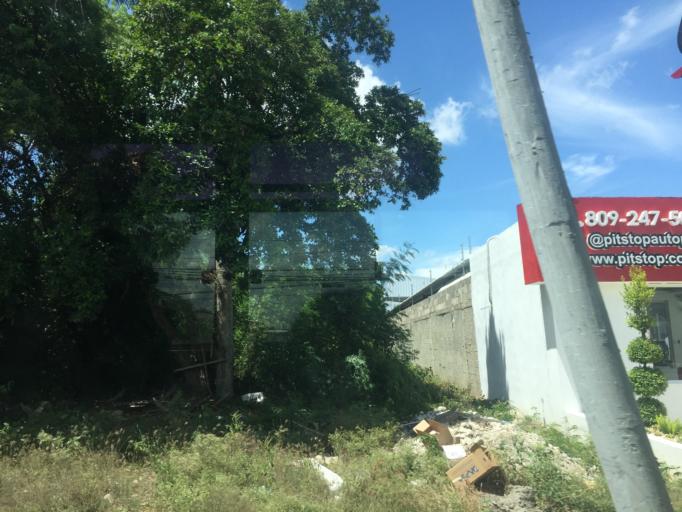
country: DO
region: Santiago
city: Santiago de los Caballeros
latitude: 19.4403
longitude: -70.7252
